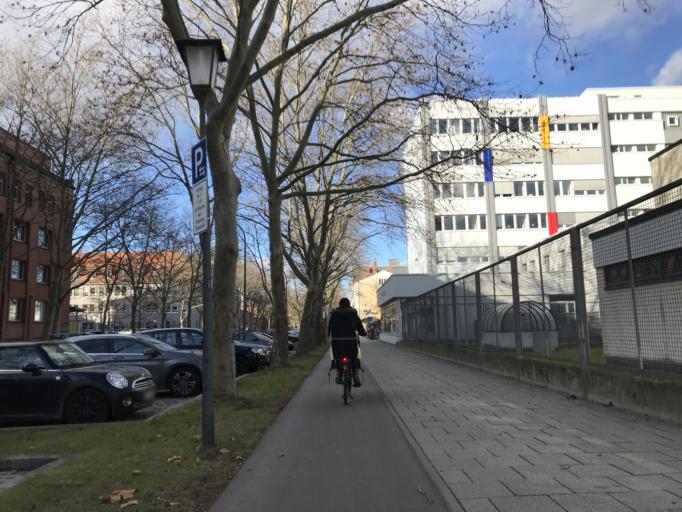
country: DE
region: Bavaria
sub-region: Upper Bavaria
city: Munich
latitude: 48.1582
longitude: 11.5570
